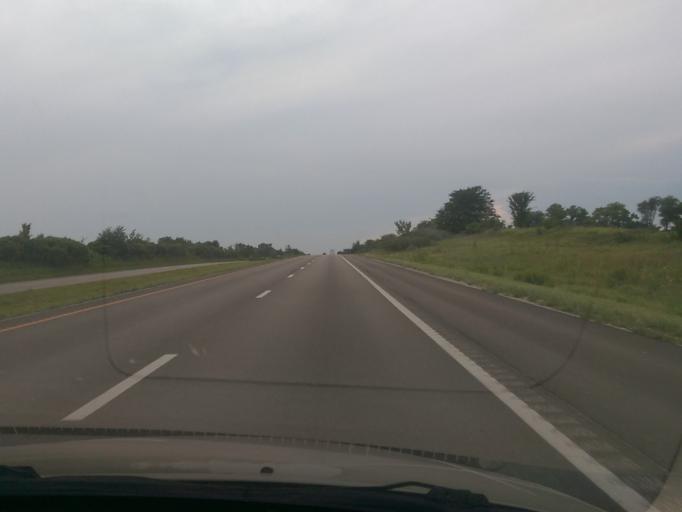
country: US
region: Missouri
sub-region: Andrew County
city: Savannah
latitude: 39.9475
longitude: -94.9456
